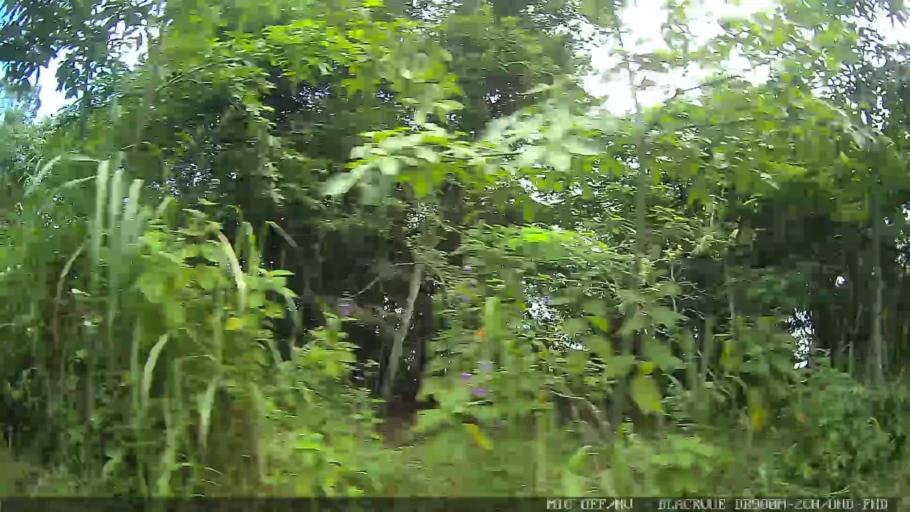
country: BR
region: Sao Paulo
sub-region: Iguape
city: Iguape
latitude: -24.6898
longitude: -47.5232
